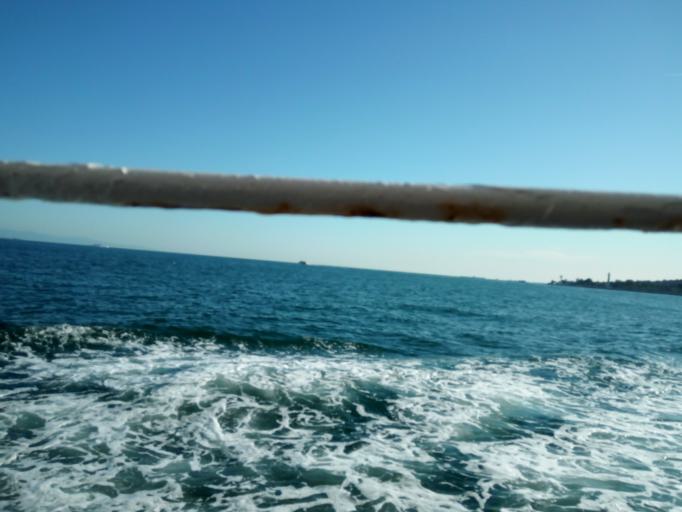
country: TR
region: Istanbul
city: Eminoenue
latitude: 41.0125
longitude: 28.9991
